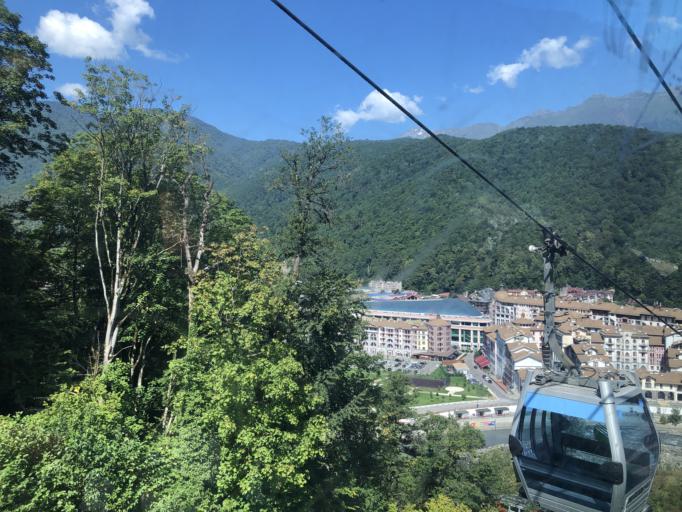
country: RU
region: Krasnodarskiy
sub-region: Sochi City
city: Krasnaya Polyana
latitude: 43.6799
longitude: 40.2651
